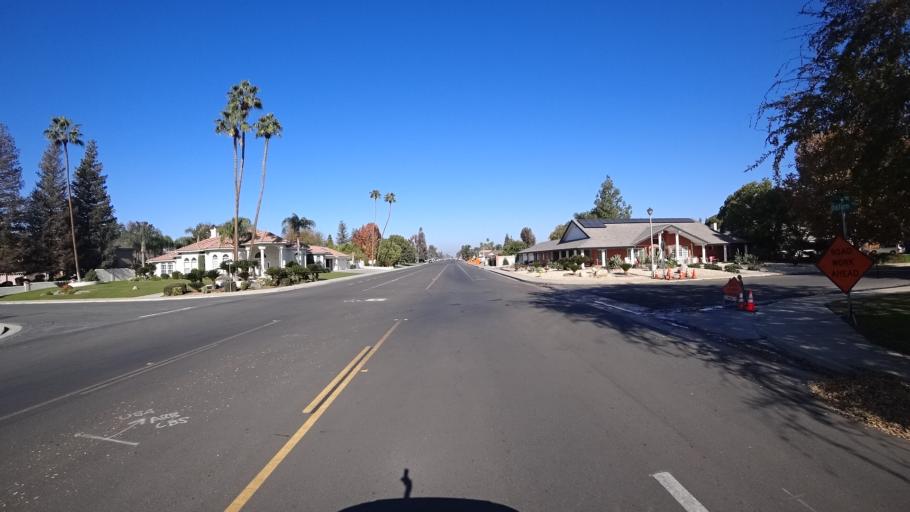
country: US
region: California
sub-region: Kern County
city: Rosedale
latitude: 35.3732
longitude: -119.1368
